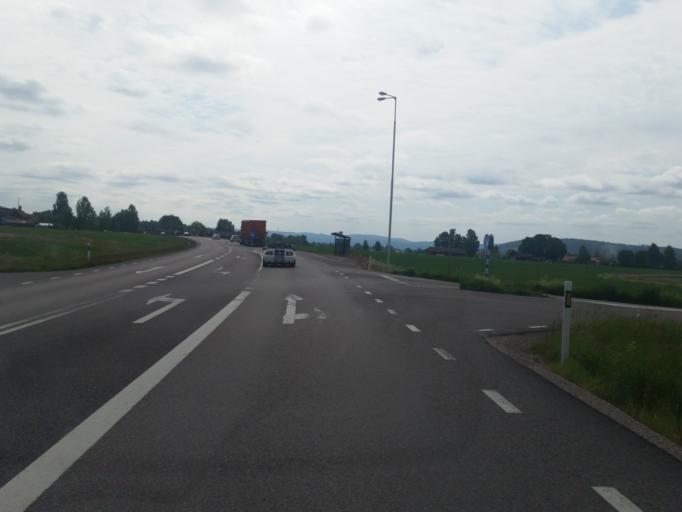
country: SE
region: Dalarna
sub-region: Gagnefs Kommun
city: Gagnef
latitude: 60.6052
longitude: 15.0526
